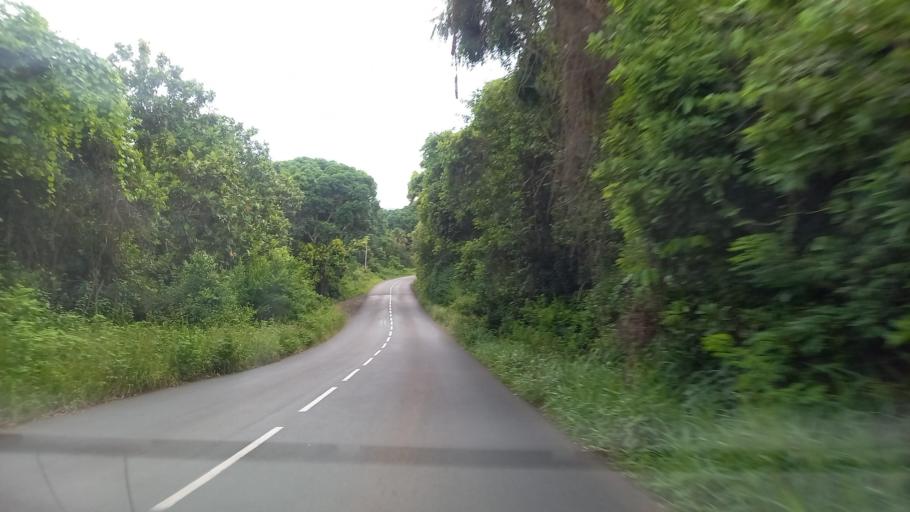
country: YT
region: M'Tsangamouji
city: M'Tsangamouji
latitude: -12.7531
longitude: 45.1123
